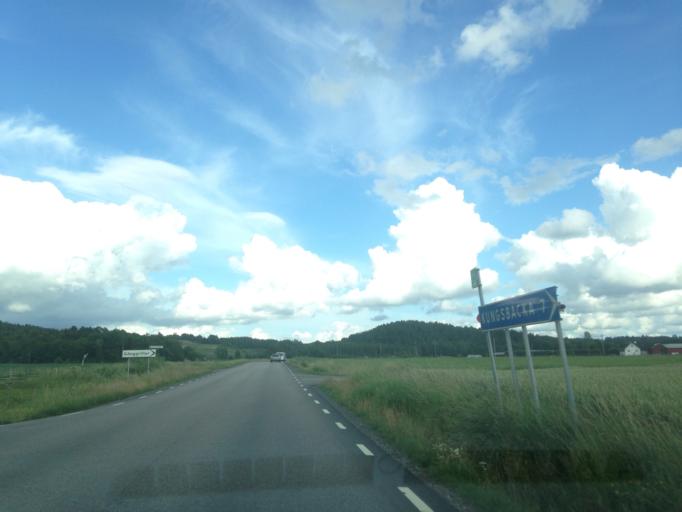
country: SE
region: Halland
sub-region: Kungsbacka Kommun
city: Fjaeras kyrkby
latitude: 57.4822
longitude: 12.1541
